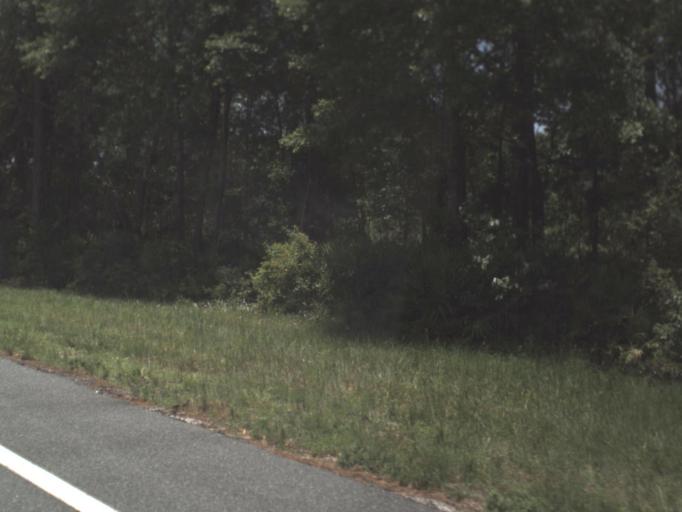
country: US
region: Florida
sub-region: Lafayette County
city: Mayo
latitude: 29.9135
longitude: -82.9518
